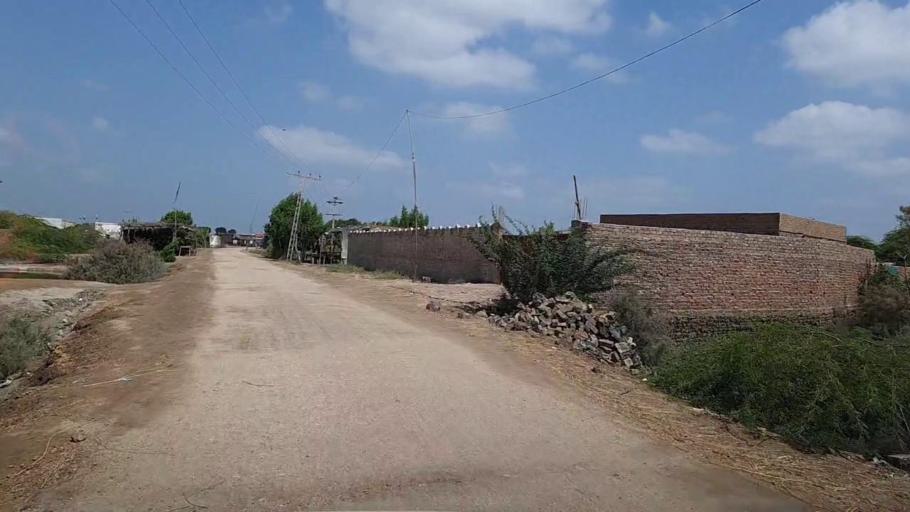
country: PK
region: Sindh
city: Kario
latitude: 24.6767
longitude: 68.5438
